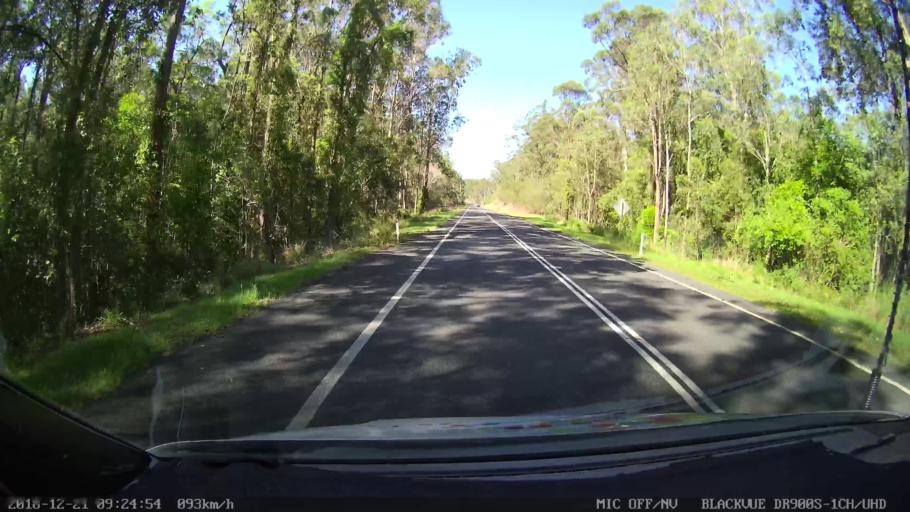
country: AU
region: New South Wales
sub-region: Clarence Valley
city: Maclean
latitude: -29.3732
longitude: 153.0134
